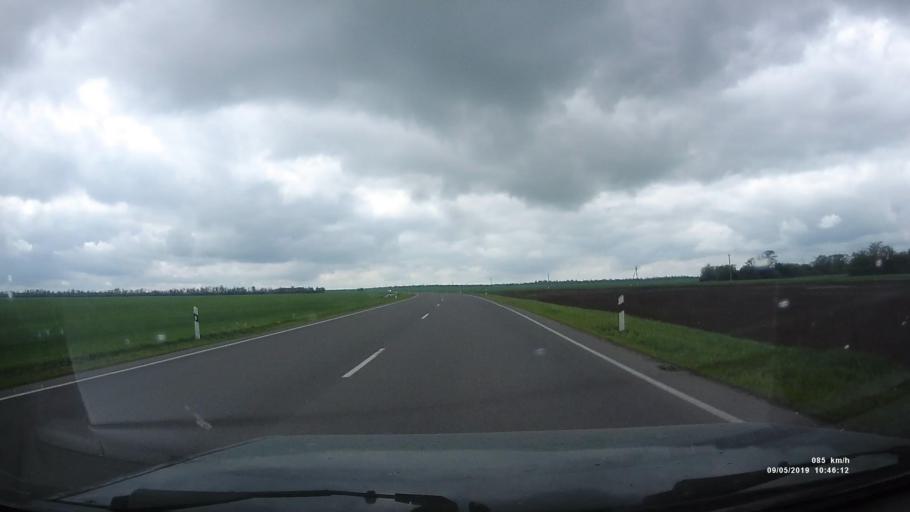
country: RU
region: Rostov
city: Peshkovo
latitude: 46.9872
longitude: 39.3576
